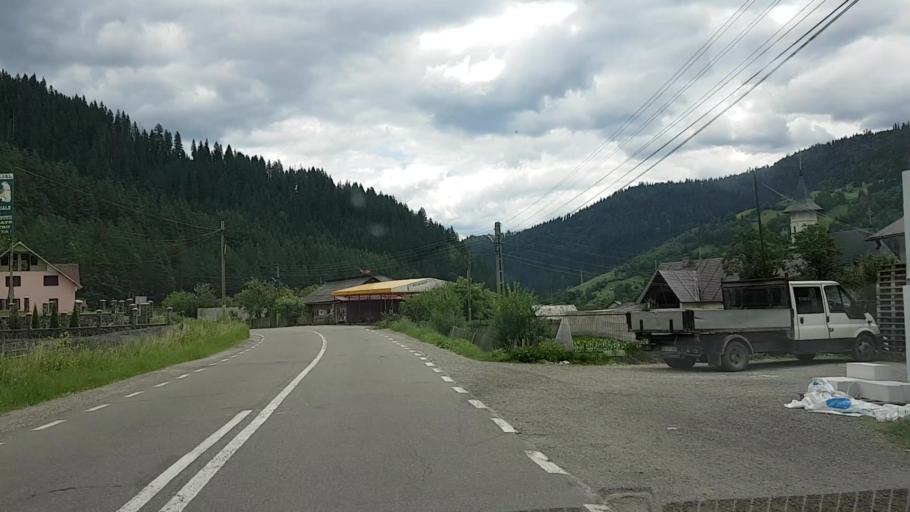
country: RO
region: Neamt
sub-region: Comuna Poiana Teiului
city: Poiana Teiului
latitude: 47.1284
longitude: 25.9030
